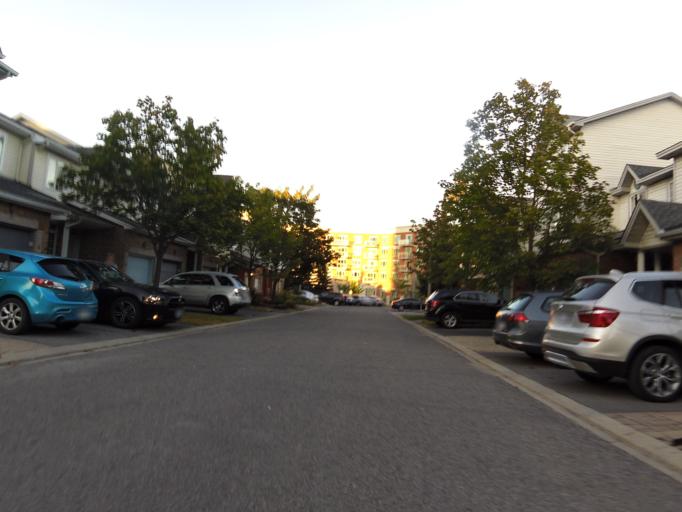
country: CA
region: Ontario
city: Ottawa
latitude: 45.4101
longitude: -75.6543
